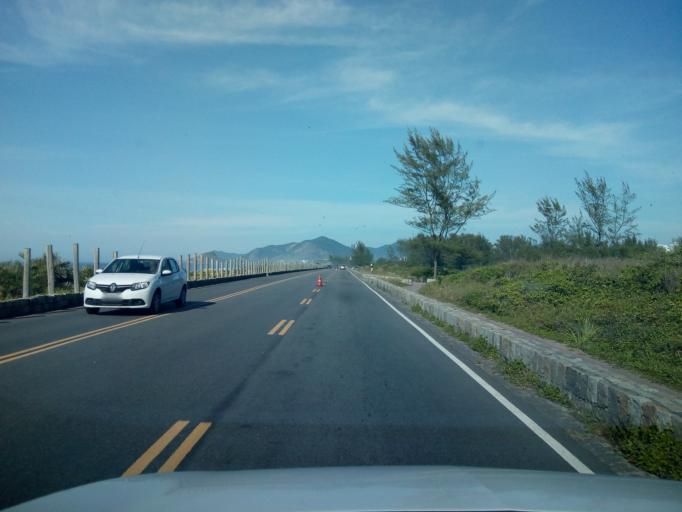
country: BR
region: Rio de Janeiro
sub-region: Nilopolis
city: Nilopolis
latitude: -23.0166
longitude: -43.4189
